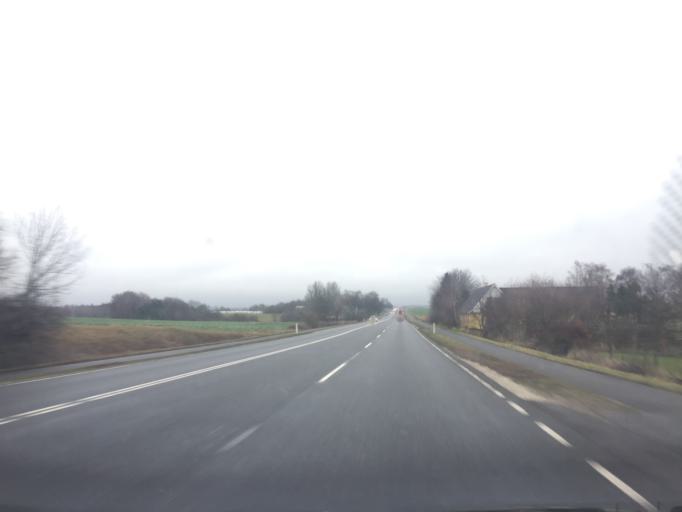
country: DK
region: Zealand
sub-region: Slagelse Kommune
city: Slagelse
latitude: 55.4204
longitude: 11.4240
